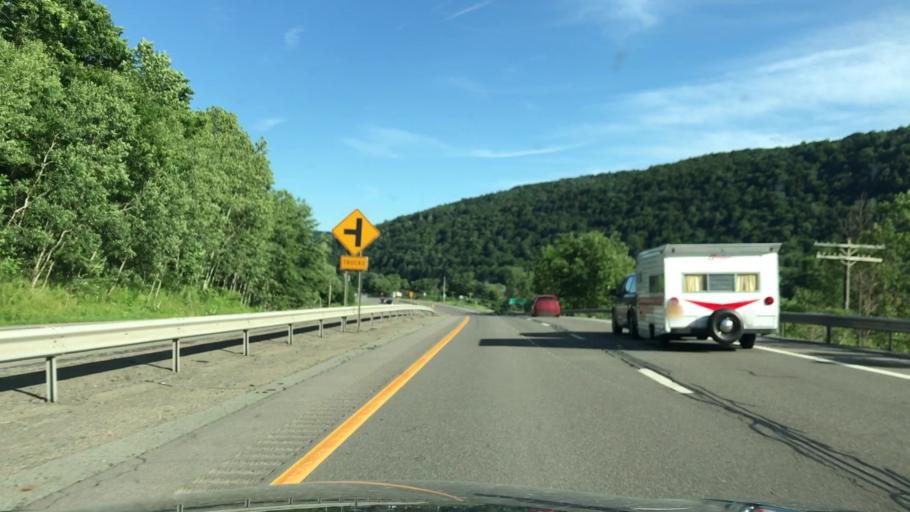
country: US
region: New York
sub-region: Broome County
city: Deposit
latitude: 42.0055
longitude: -75.3613
